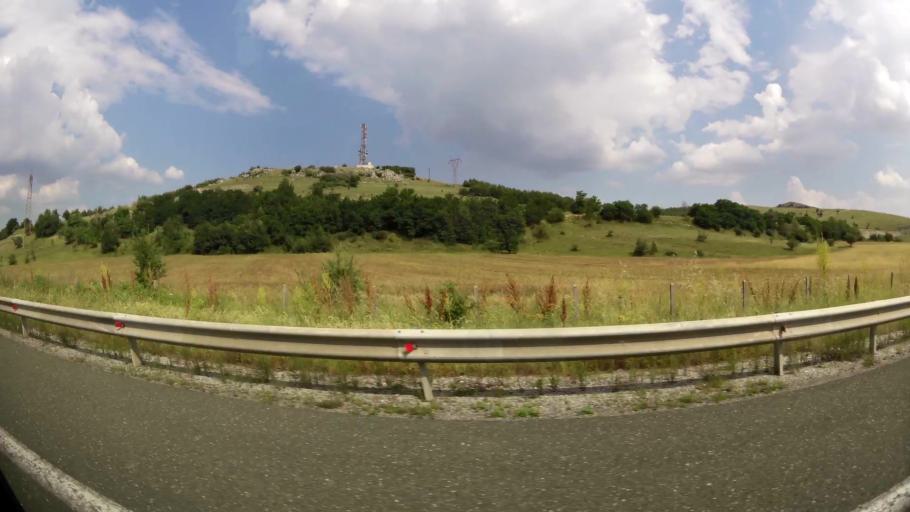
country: GR
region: West Macedonia
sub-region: Nomos Kozanis
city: Koila
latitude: 40.3573
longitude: 21.8144
